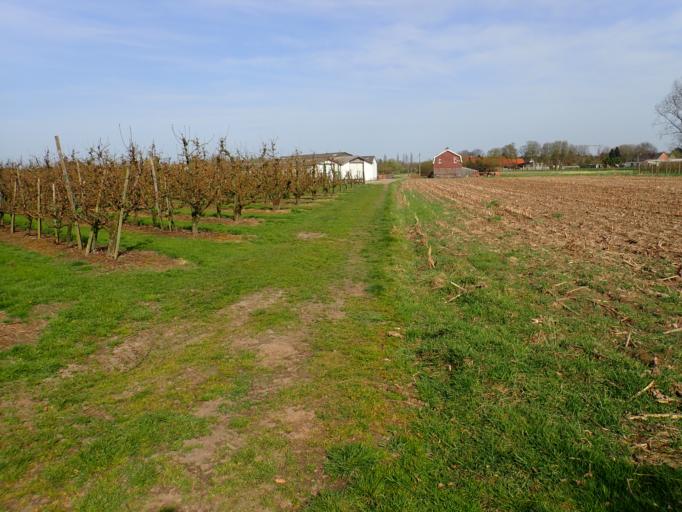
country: BE
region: Flanders
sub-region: Provincie Antwerpen
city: Ranst
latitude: 51.1669
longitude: 4.6059
